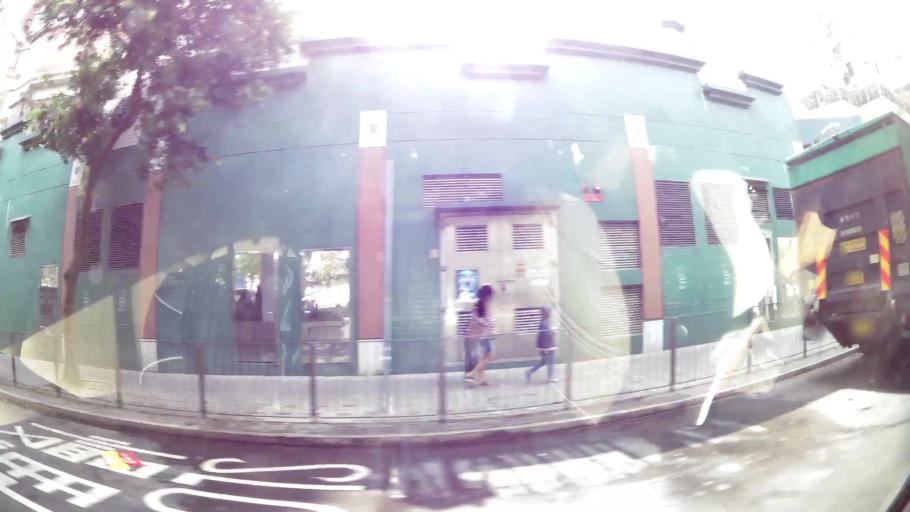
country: HK
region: Wanchai
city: Wan Chai
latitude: 22.2811
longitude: 114.2305
